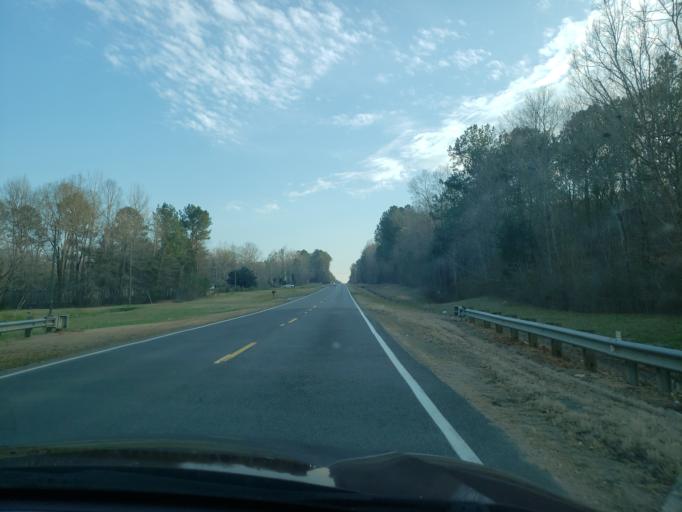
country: US
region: Alabama
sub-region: Hale County
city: Greensboro
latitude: 32.7600
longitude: -87.5853
